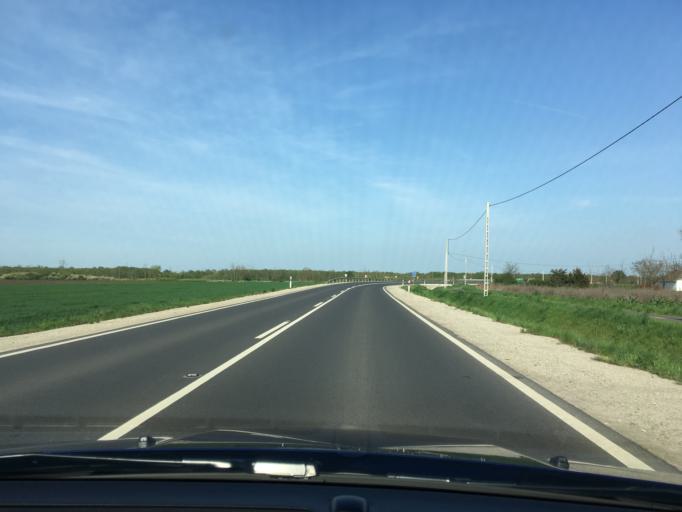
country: HU
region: Bekes
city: Csorvas
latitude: 46.6457
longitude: 20.8676
